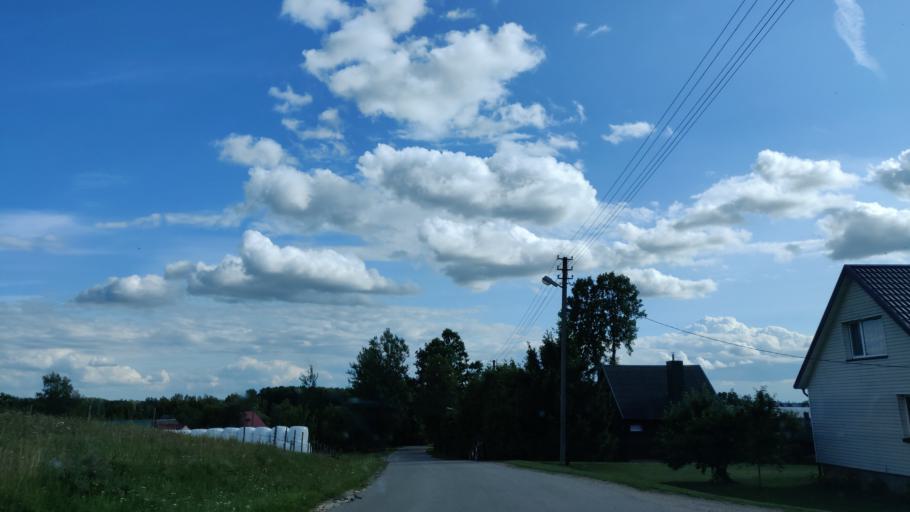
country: LT
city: Varniai
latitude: 55.5976
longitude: 22.3108
